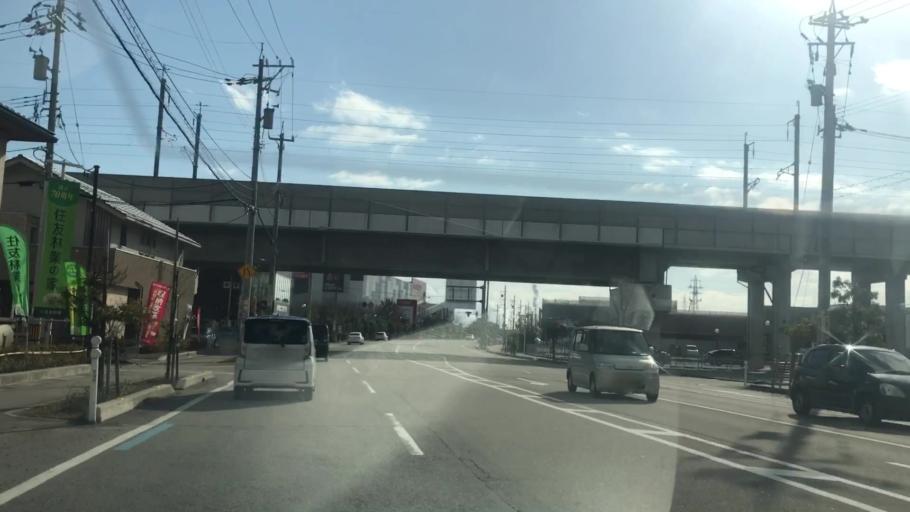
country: JP
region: Toyama
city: Takaoka
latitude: 36.7273
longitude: 137.0154
